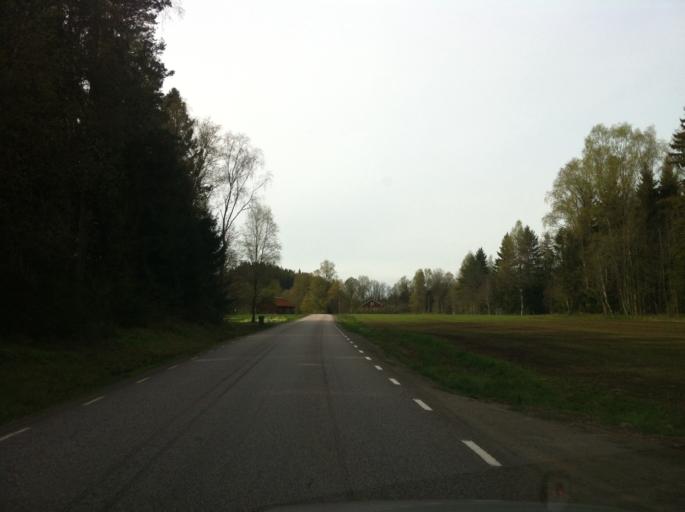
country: SE
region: Vaestra Goetaland
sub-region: Bollebygds Kommun
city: Bollebygd
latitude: 57.5778
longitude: 12.5631
